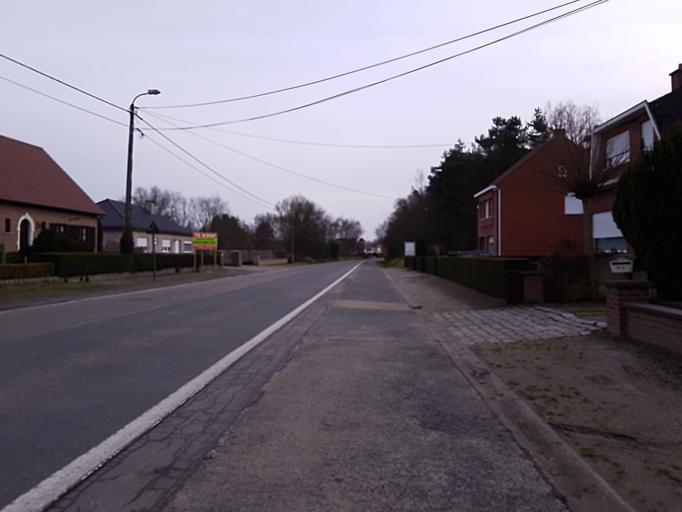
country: BE
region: Flanders
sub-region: Provincie Antwerpen
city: Putte
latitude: 51.0507
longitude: 4.6812
